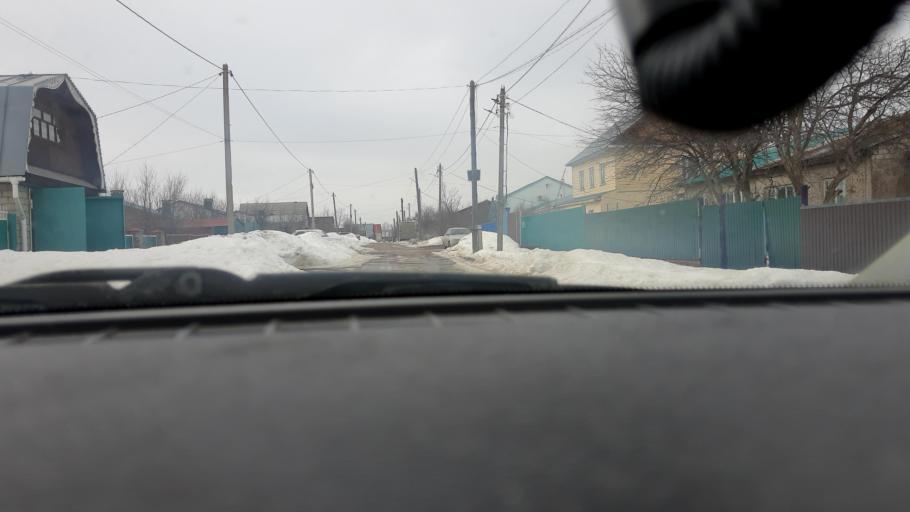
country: RU
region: Bashkortostan
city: Avdon
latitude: 54.6102
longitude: 55.8588
